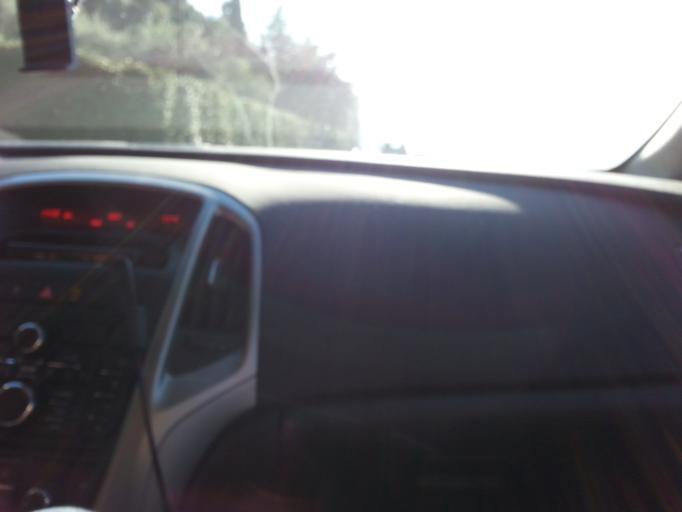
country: IT
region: Trentino-Alto Adige
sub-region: Provincia di Trento
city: Torbole sul Garda
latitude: 45.8662
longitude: 10.8765
